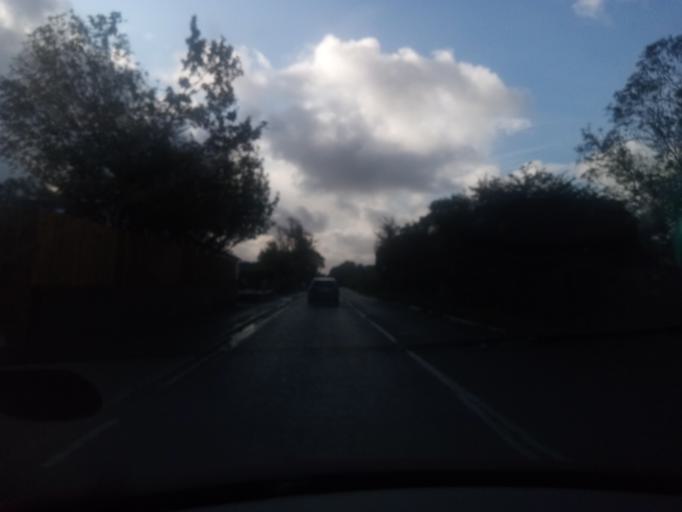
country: GB
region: England
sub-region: Cumbria
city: Carlisle
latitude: 54.9494
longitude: -2.9432
